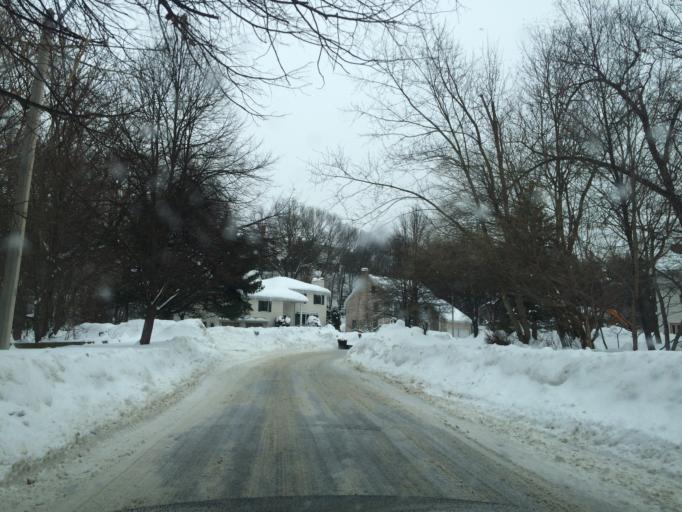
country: US
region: Massachusetts
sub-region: Middlesex County
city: Waltham
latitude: 42.3968
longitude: -71.2247
